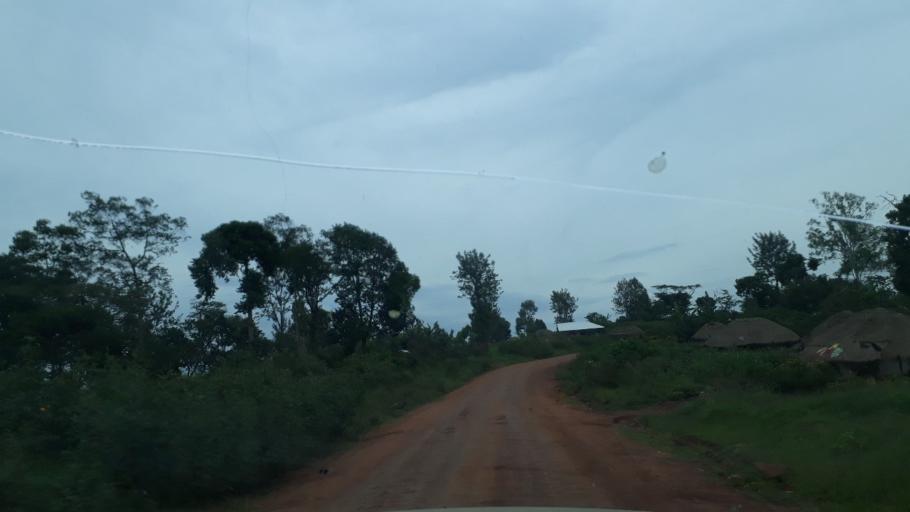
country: UG
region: Northern Region
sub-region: Zombo District
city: Paidha
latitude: 2.1798
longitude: 30.7199
